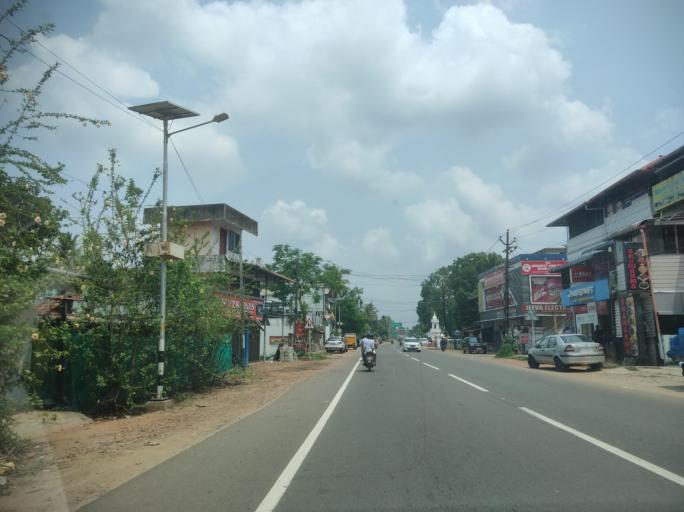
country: IN
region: Kerala
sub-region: Kottayam
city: Changanacheri
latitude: 9.4266
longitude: 76.5459
